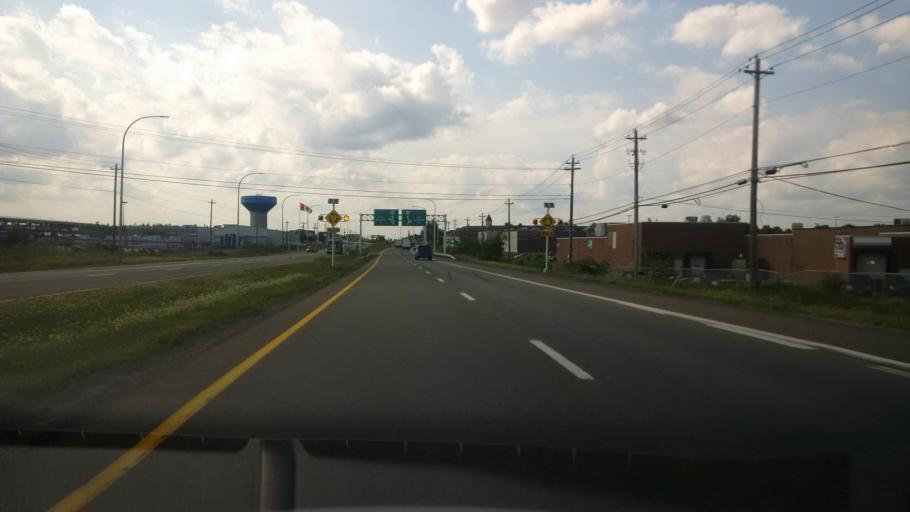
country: CA
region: New Brunswick
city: Fredericton
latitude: 45.9392
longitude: -66.6655
